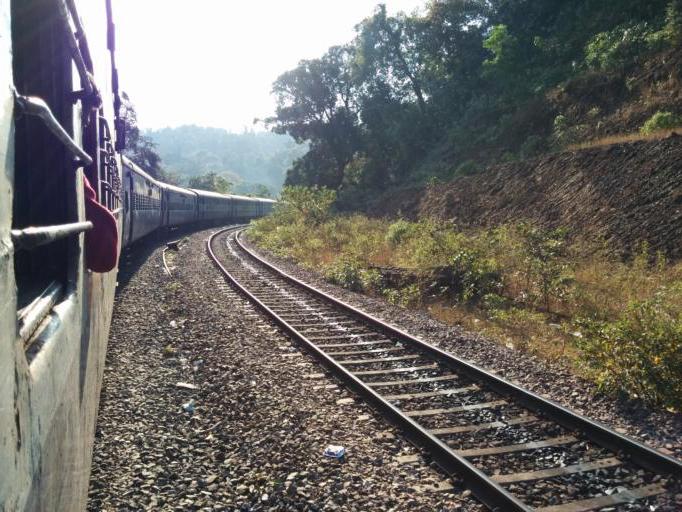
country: IN
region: Goa
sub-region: South Goa
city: Sanguem
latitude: 15.3109
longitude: 74.2955
